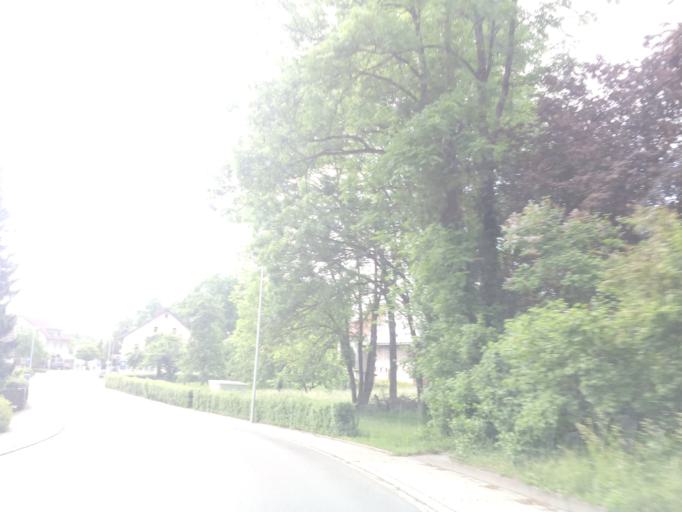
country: DE
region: Bavaria
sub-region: Upper Franconia
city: Weitramsdorf
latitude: 50.2653
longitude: 10.9070
